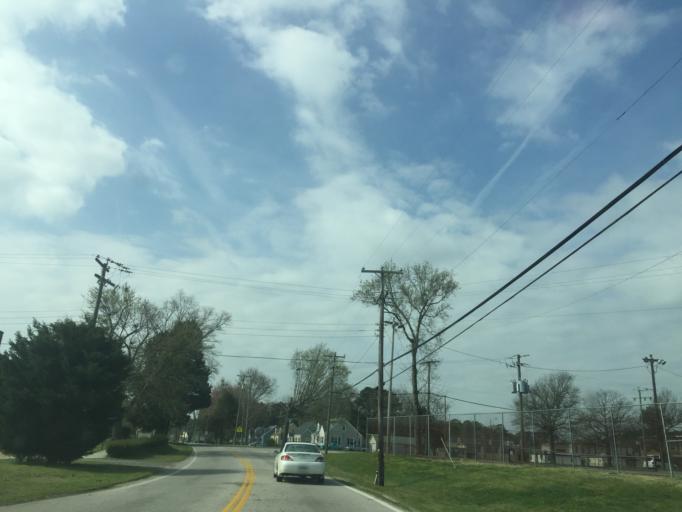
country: US
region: Virginia
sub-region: City of Newport News
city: Newport News
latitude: 37.0542
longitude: -76.4725
